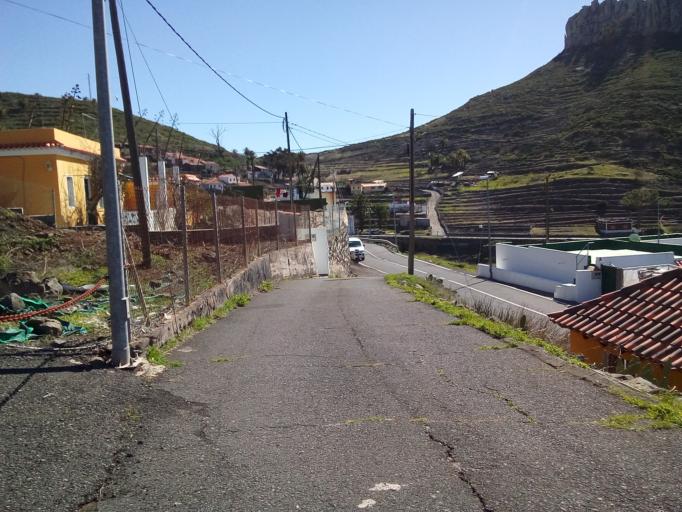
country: ES
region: Canary Islands
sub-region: Provincia de Santa Cruz de Tenerife
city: Alajero
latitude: 28.1058
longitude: -17.2763
